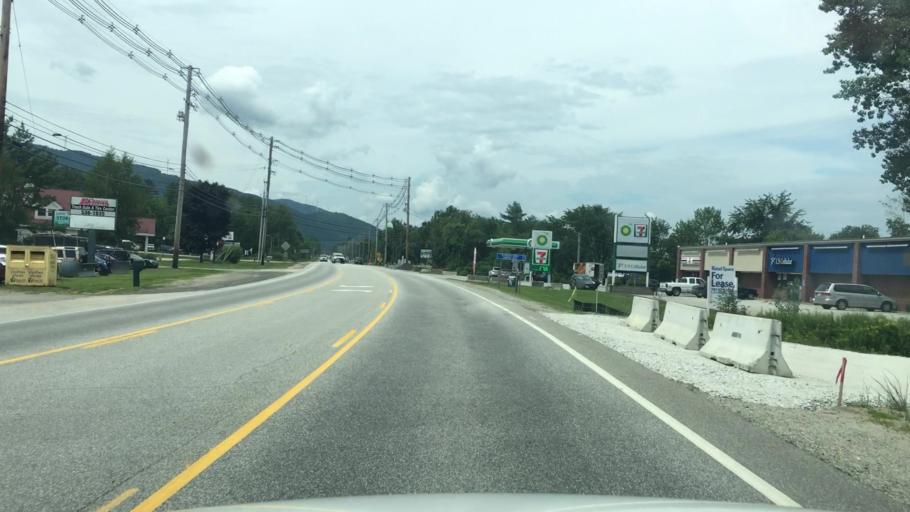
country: US
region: New Hampshire
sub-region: Grafton County
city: Plymouth
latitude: 43.7713
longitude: -71.7254
